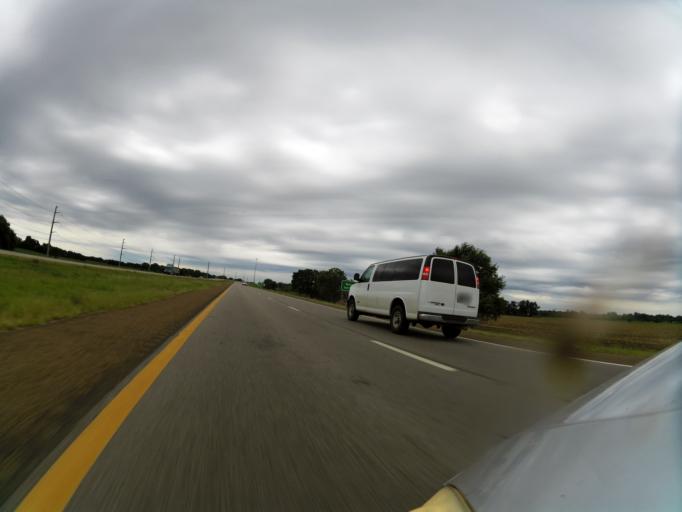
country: US
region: Kansas
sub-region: Sedgwick County
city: Maize
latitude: 37.7882
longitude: -97.4698
